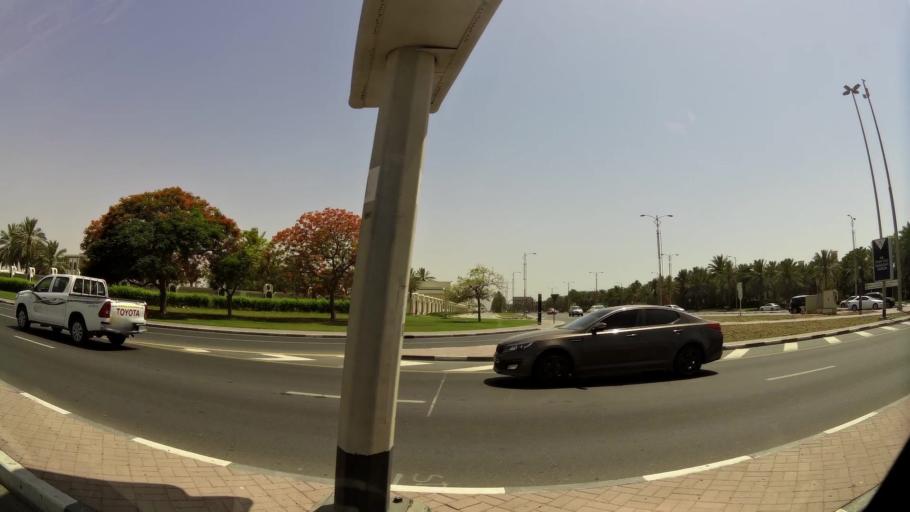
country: AE
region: Dubai
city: Dubai
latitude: 25.1325
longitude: 55.1887
